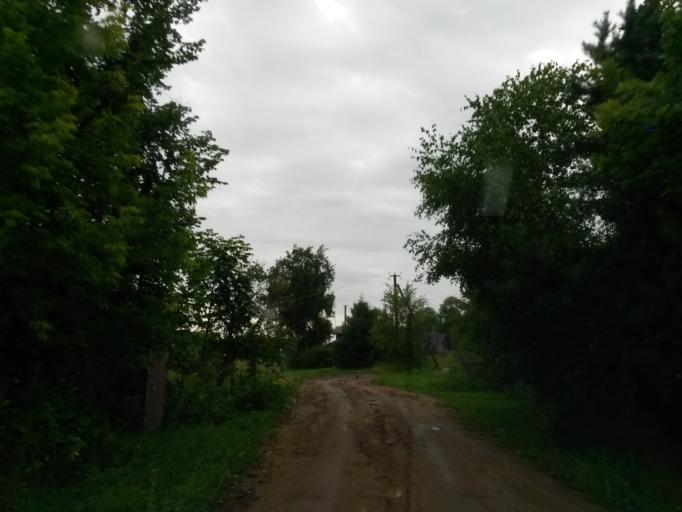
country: RU
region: Jaroslavl
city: Tutayev
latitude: 57.9476
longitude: 39.4438
